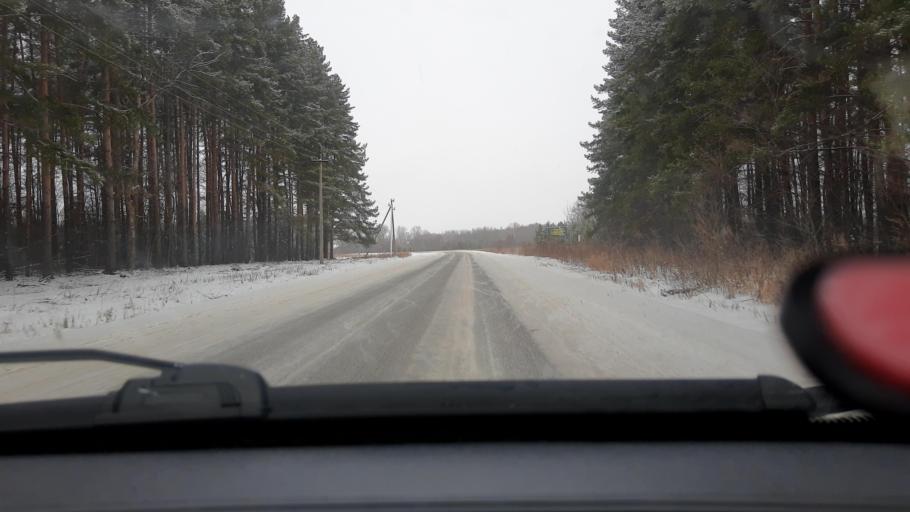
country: RU
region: Bashkortostan
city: Iglino
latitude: 54.6779
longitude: 56.4181
